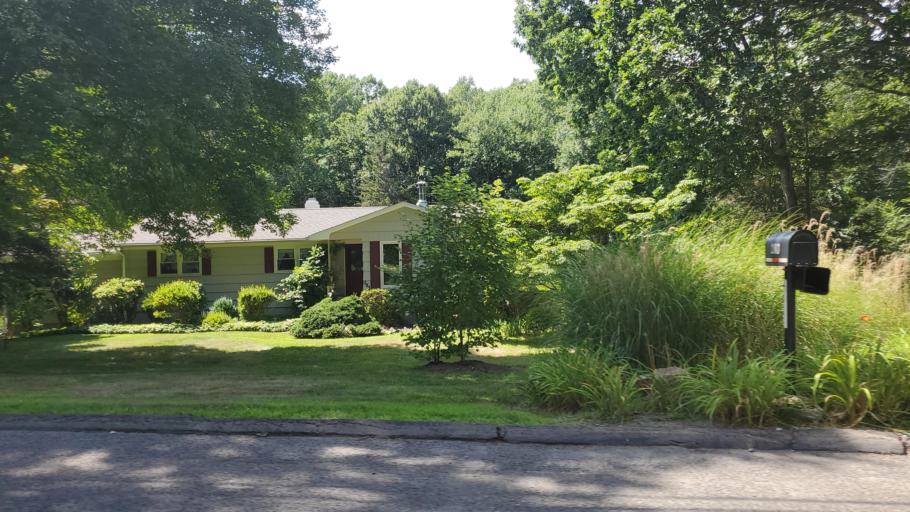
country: US
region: Connecticut
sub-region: Fairfield County
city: Newtown
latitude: 41.3454
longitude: -73.2785
